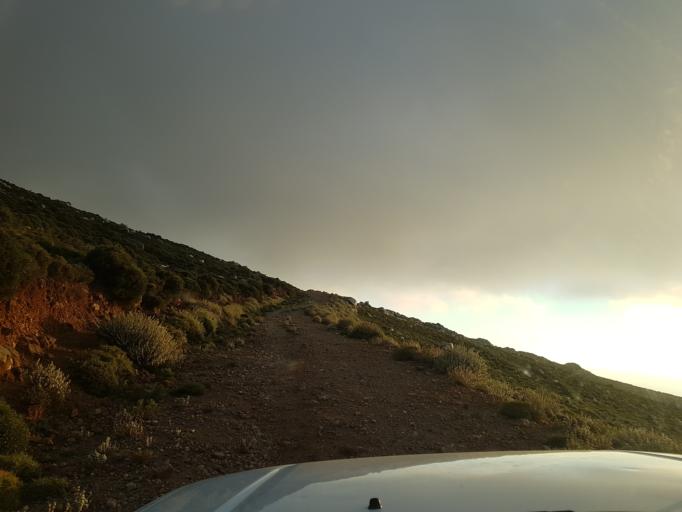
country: GR
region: Crete
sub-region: Nomos Chanias
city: Vryses
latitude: 35.4466
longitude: 23.5935
